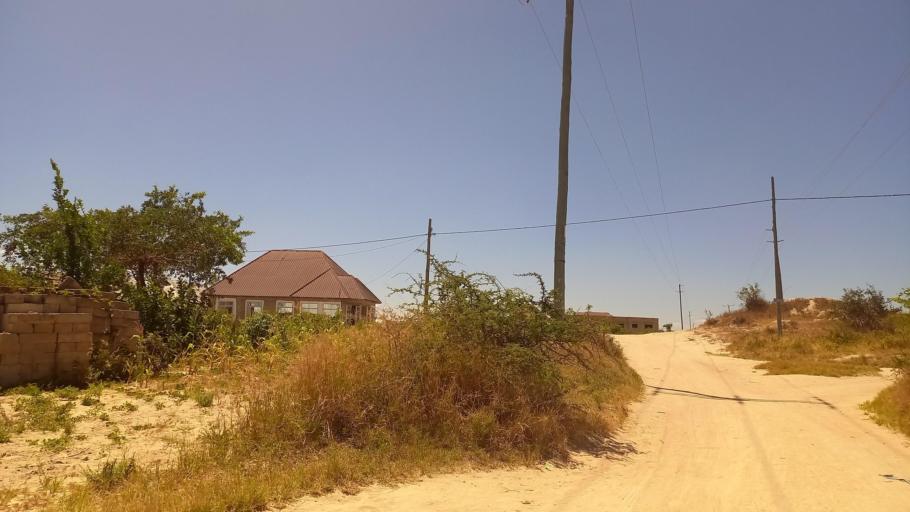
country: TZ
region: Dodoma
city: Dodoma
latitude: -6.1361
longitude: 35.7083
